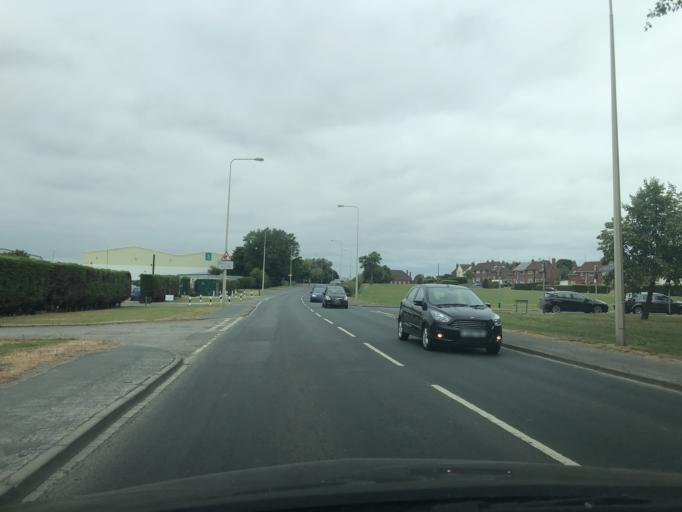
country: GB
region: England
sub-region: North Yorkshire
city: Scarborough
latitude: 54.2384
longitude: -0.4039
